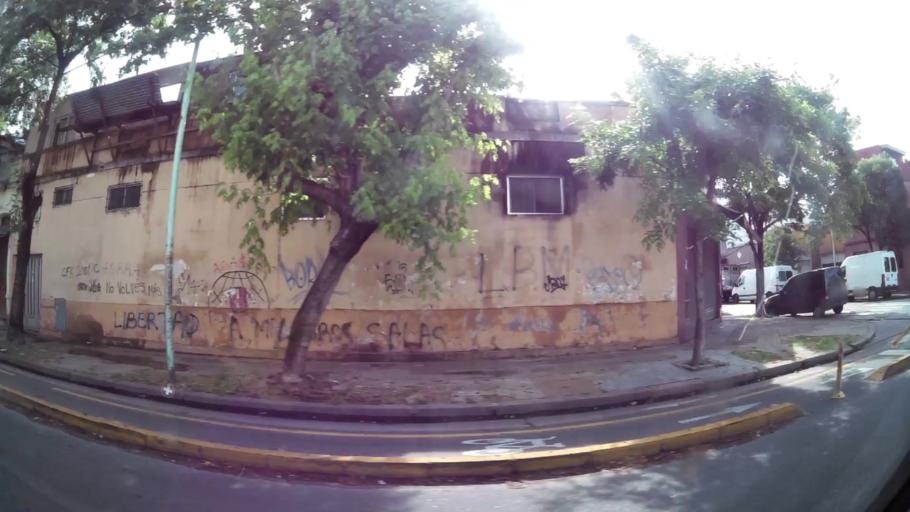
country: AR
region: Buenos Aires F.D.
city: Buenos Aires
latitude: -34.6409
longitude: -58.4182
